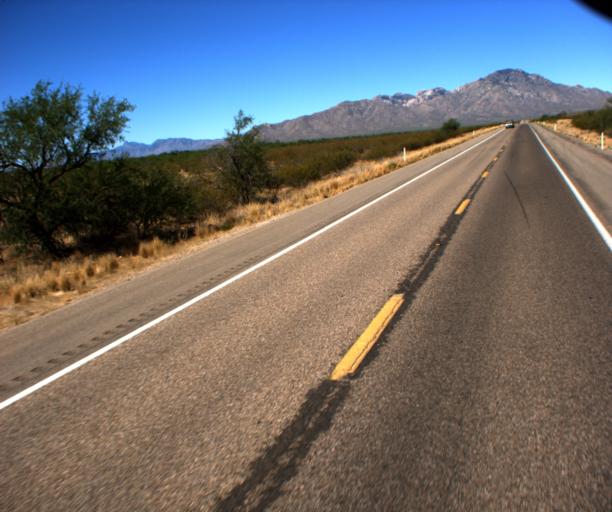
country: US
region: Arizona
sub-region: Pima County
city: Three Points
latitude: 32.0544
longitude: -111.4103
